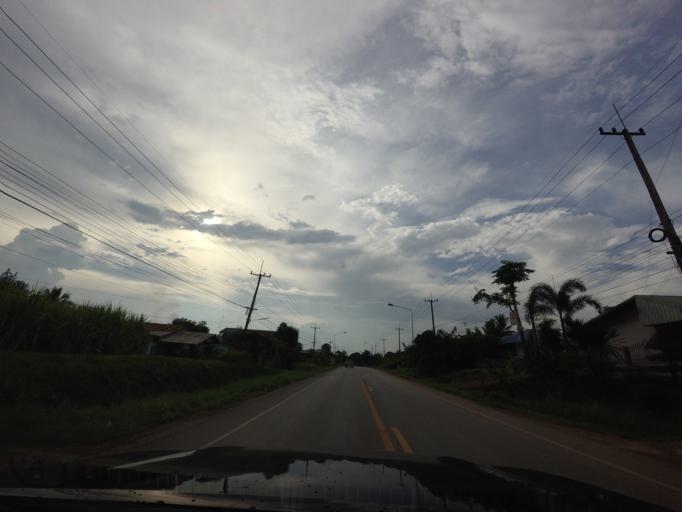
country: TH
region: Changwat Udon Thani
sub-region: Amphoe Ban Phue
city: Ban Phue
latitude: 17.7030
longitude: 102.4355
